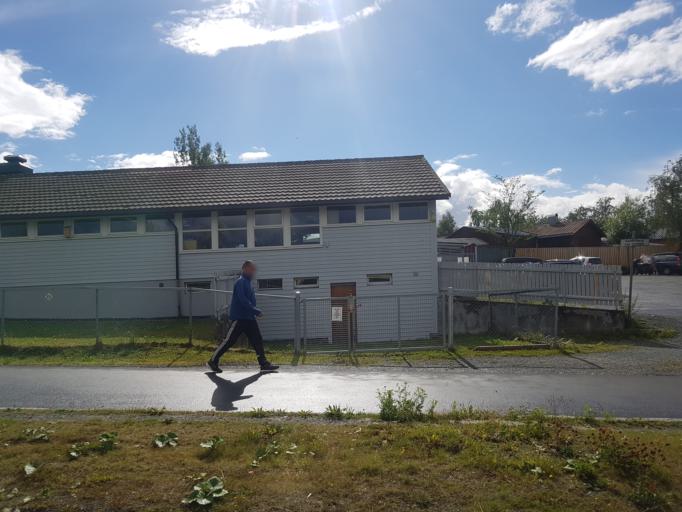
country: NO
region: Sor-Trondelag
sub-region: Trondheim
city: Trondheim
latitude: 63.4166
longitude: 10.4620
